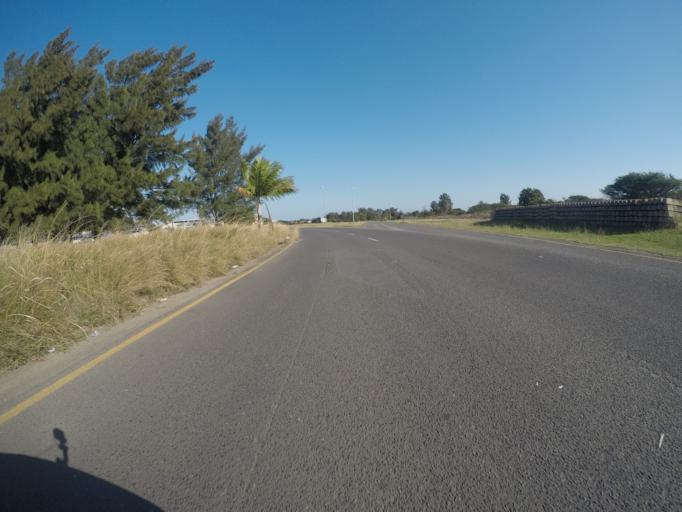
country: ZA
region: KwaZulu-Natal
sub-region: uThungulu District Municipality
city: Richards Bay
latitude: -28.7913
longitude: 32.0776
